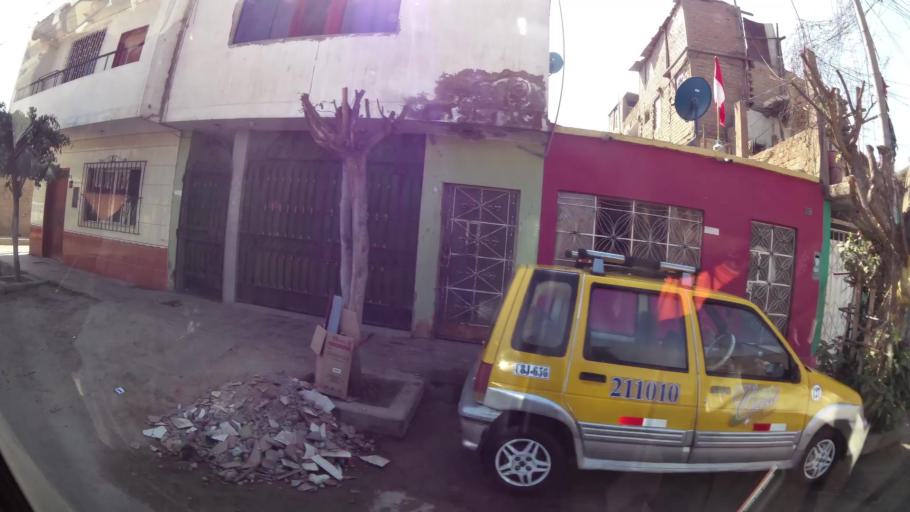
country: PE
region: Ica
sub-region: Provincia de Ica
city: Ica
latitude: -14.0662
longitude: -75.7222
